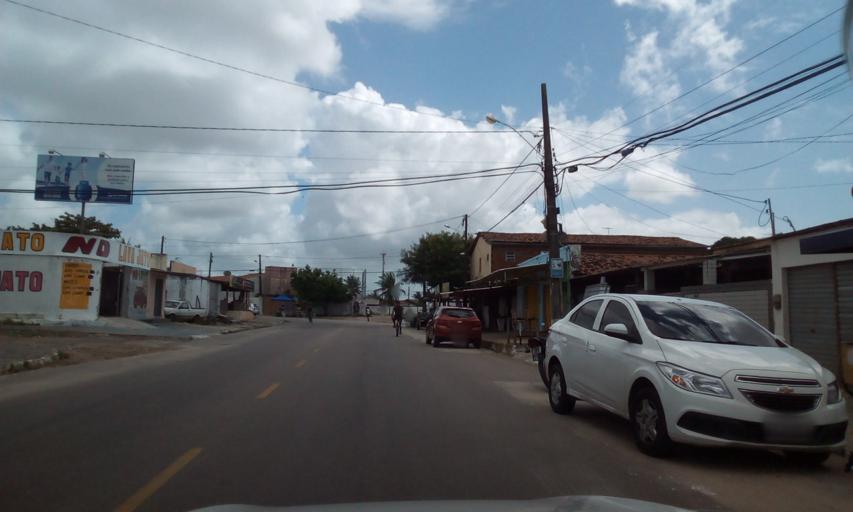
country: BR
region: Paraiba
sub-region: Conde
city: Conde
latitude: -7.2054
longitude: -34.8398
